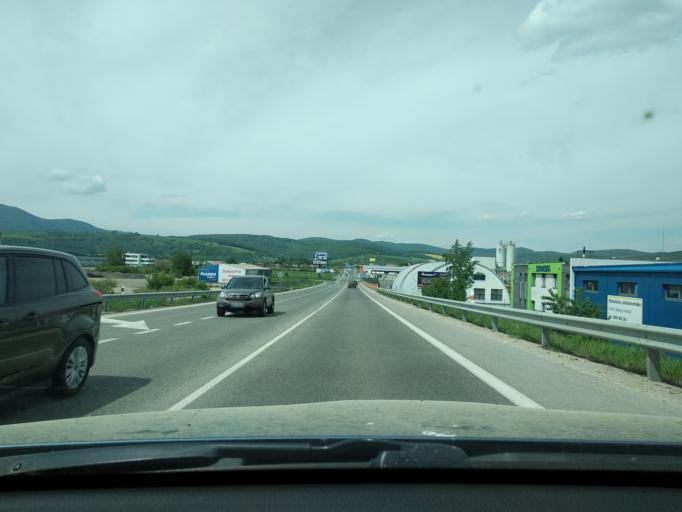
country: SK
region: Trenciansky
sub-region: Okres Trencin
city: Trencin
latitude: 48.8870
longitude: 18.0100
